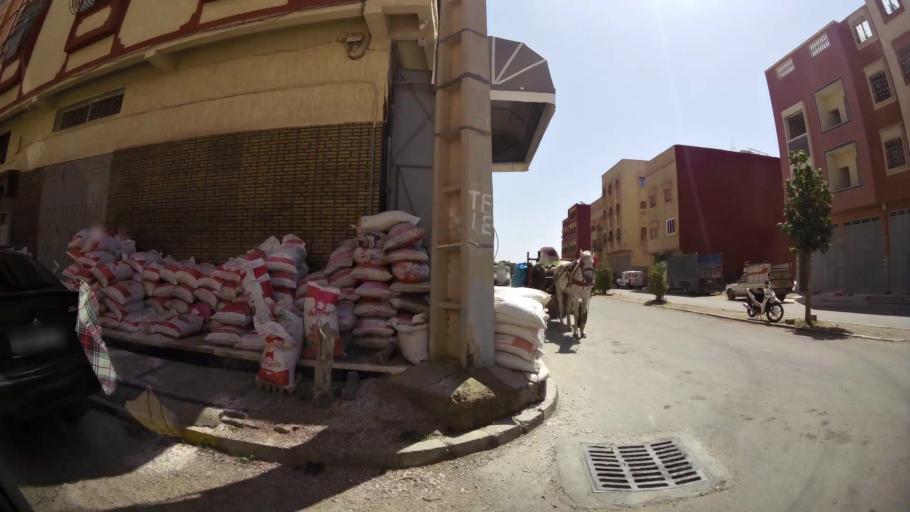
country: MA
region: Souss-Massa-Draa
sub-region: Inezgane-Ait Mellou
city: Inezgane
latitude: 30.3296
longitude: -9.5050
